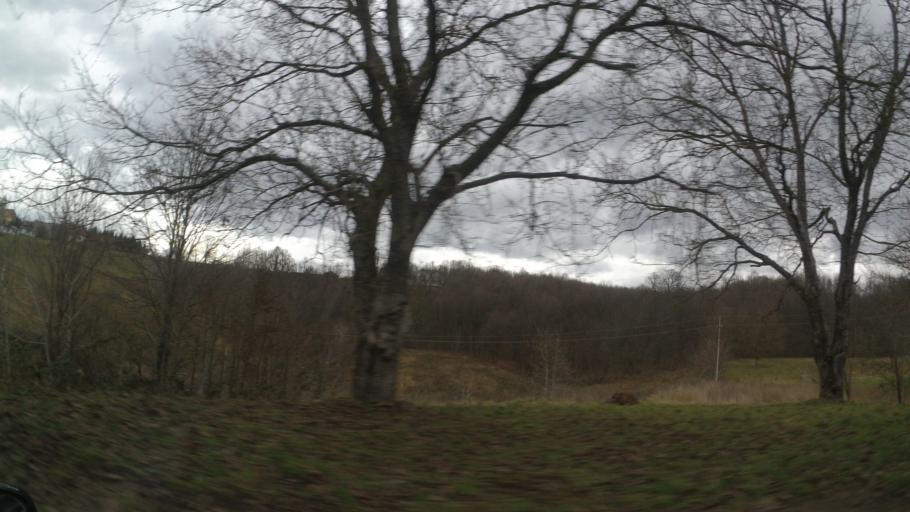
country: HR
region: Karlovacka
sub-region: Grad Karlovac
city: Karlovac
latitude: 45.3922
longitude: 15.5265
